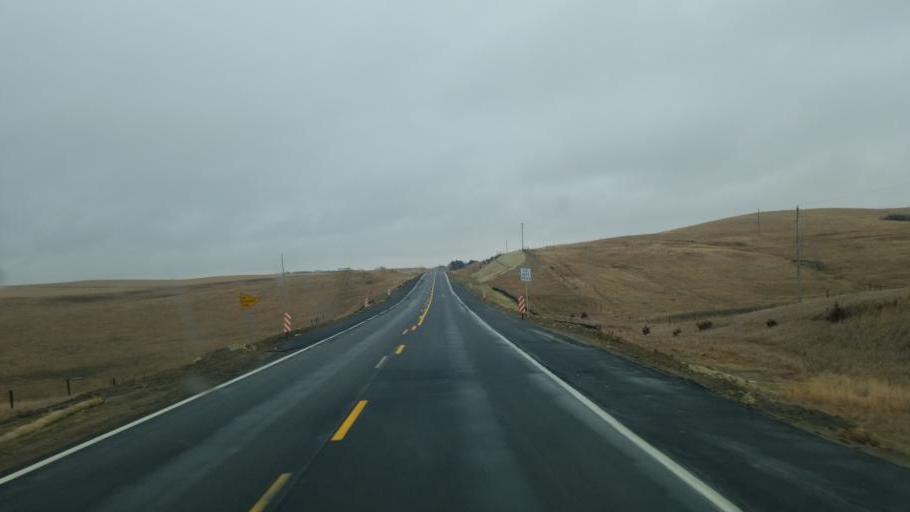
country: US
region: Nebraska
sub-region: Knox County
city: Center
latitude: 42.5971
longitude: -97.8293
